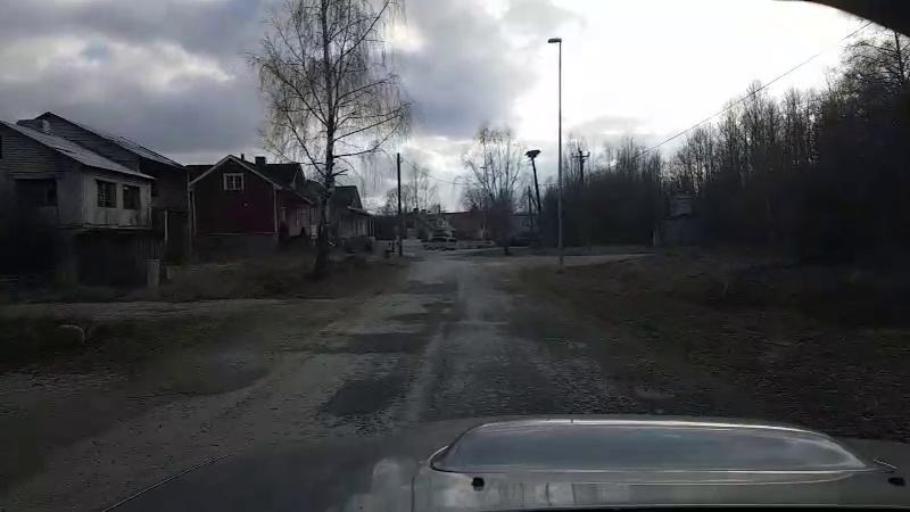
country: EE
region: Jaervamaa
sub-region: Paide linn
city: Paide
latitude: 58.8830
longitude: 25.5291
